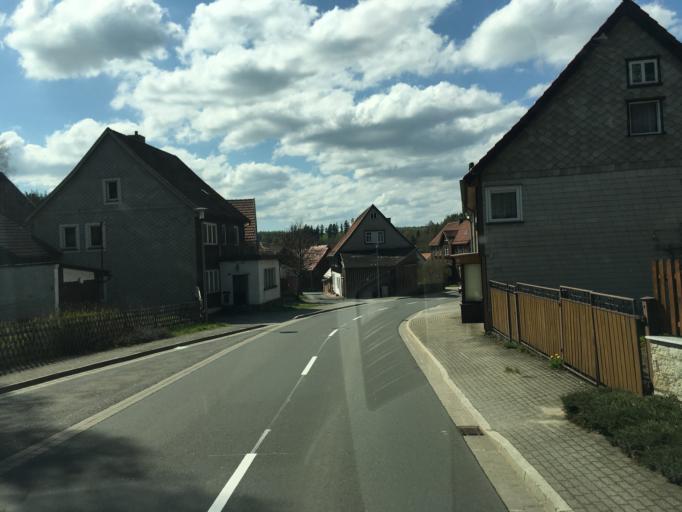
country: DE
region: Saxony-Anhalt
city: Hasselfelde
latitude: 51.6853
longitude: 10.7897
